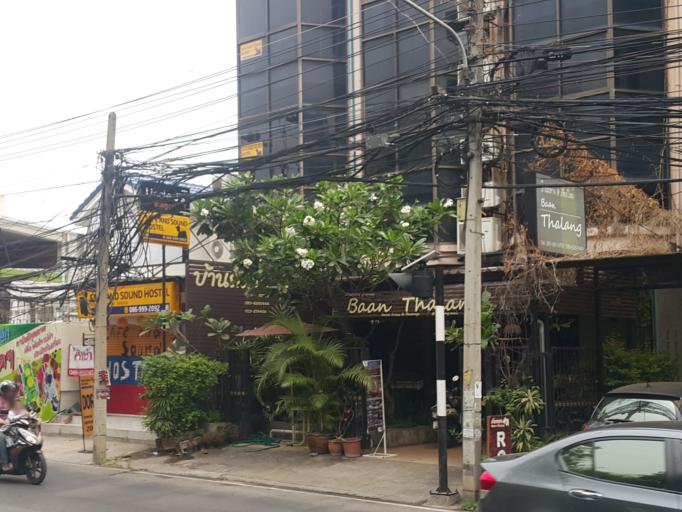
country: TH
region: Chiang Mai
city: Chiang Mai
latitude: 18.7979
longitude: 98.9791
